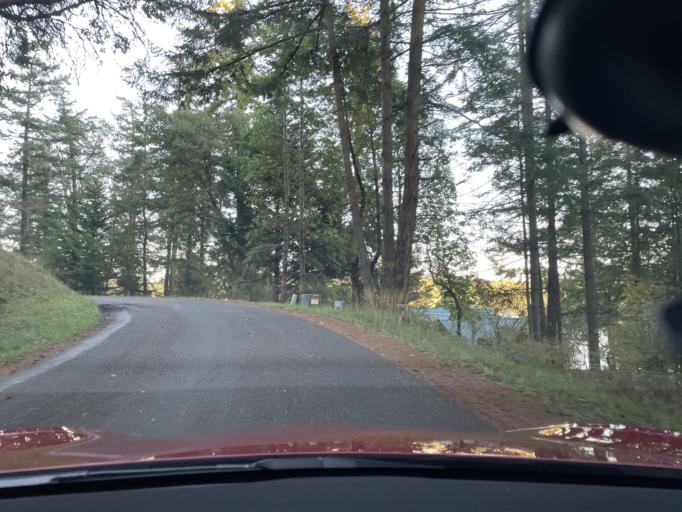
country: US
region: Washington
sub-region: San Juan County
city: Friday Harbor
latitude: 48.5999
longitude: -123.1511
